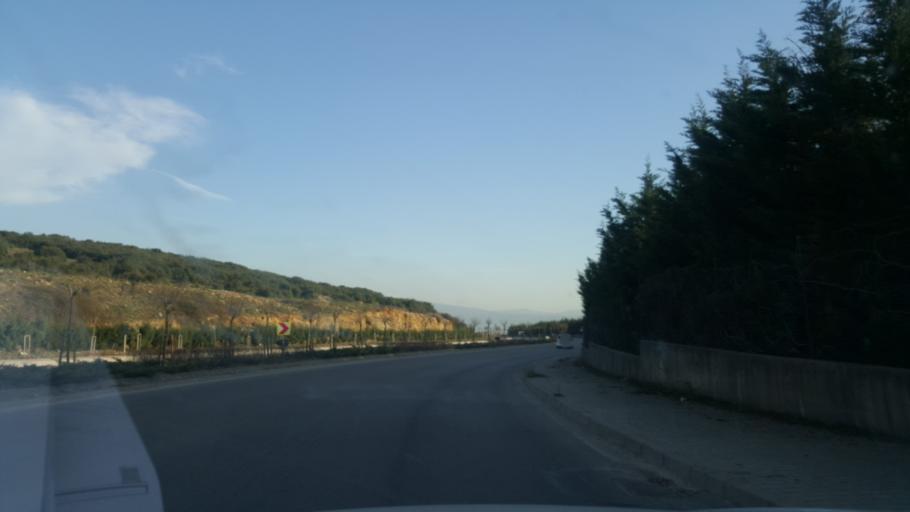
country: TR
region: Kocaeli
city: Tavsancil
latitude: 40.8168
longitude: 29.5657
